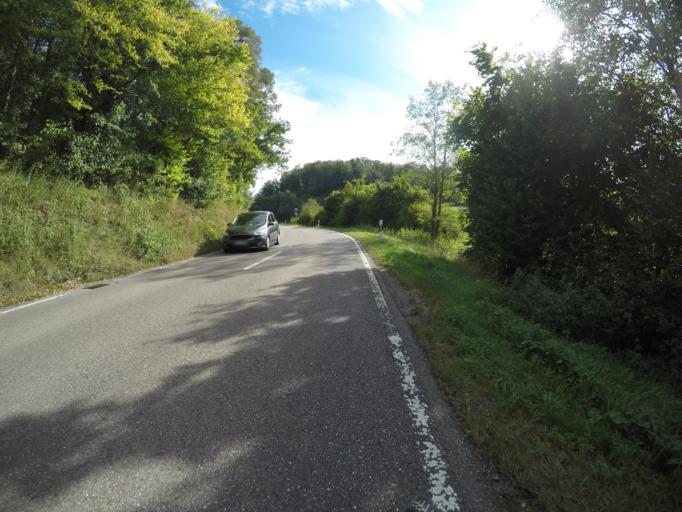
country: DE
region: Baden-Wuerttemberg
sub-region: Regierungsbezirk Stuttgart
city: Weissach
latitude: 48.8499
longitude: 8.9604
